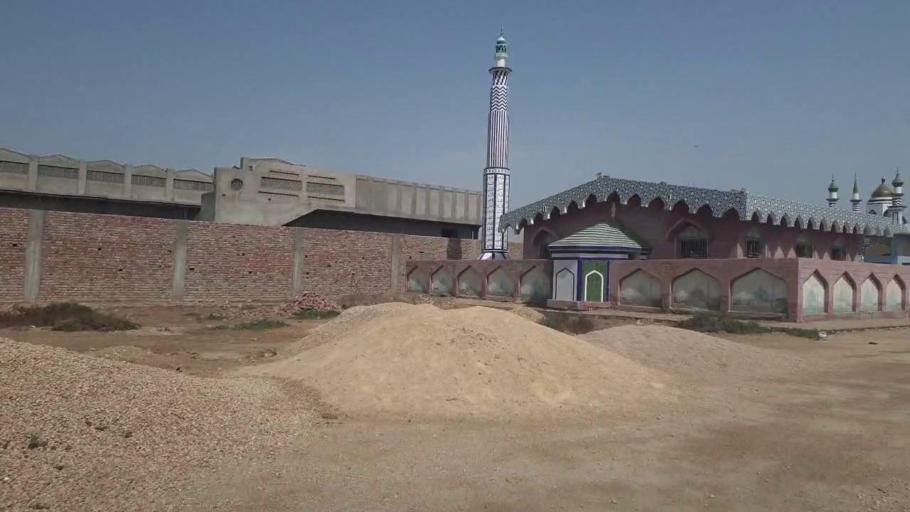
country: PK
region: Sindh
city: Dhoro Naro
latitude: 25.3711
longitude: 69.5898
